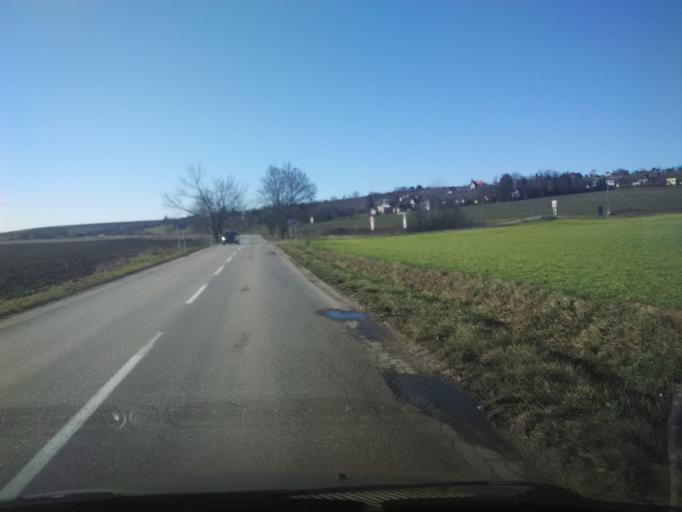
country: SK
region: Nitriansky
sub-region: Okres Nitra
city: Vrable
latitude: 48.2497
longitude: 18.2932
